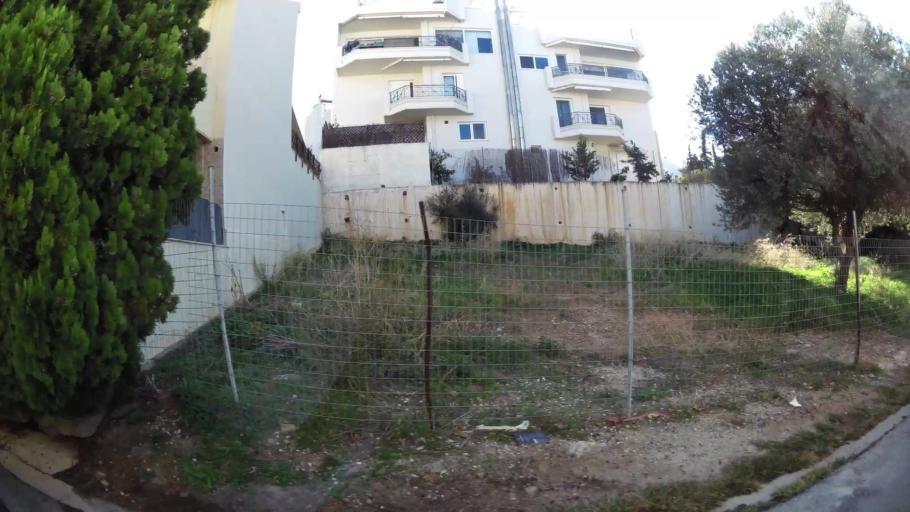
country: GR
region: Attica
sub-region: Nomarchia Anatolikis Attikis
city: Voula
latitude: 37.8549
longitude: 23.7717
